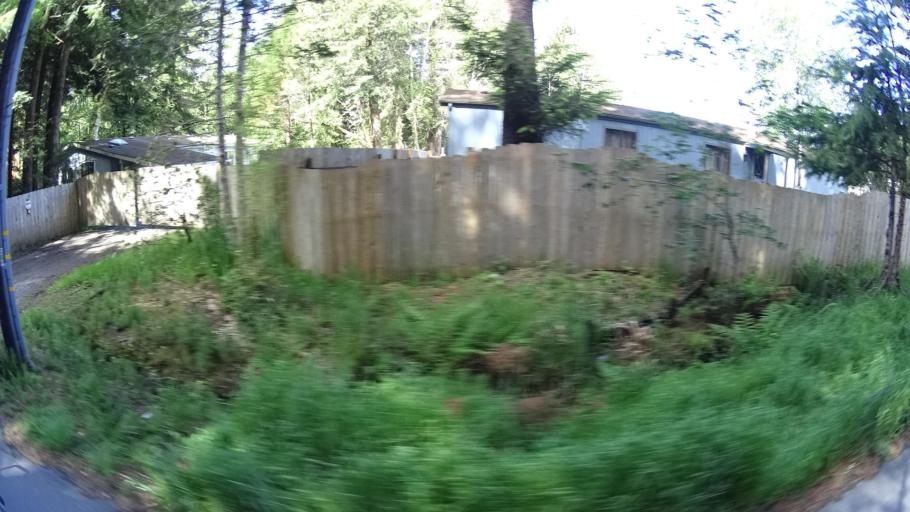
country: US
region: California
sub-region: Humboldt County
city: McKinleyville
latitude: 40.9323
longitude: -124.0816
